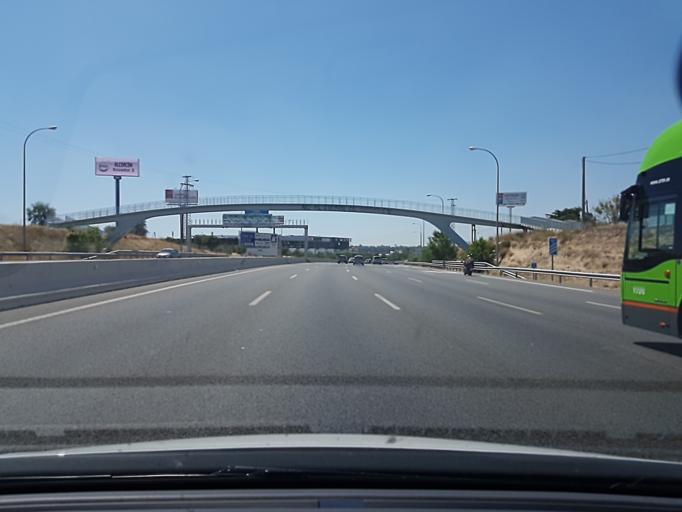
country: ES
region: Madrid
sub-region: Provincia de Madrid
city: Leganes
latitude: 40.3594
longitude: -3.7708
